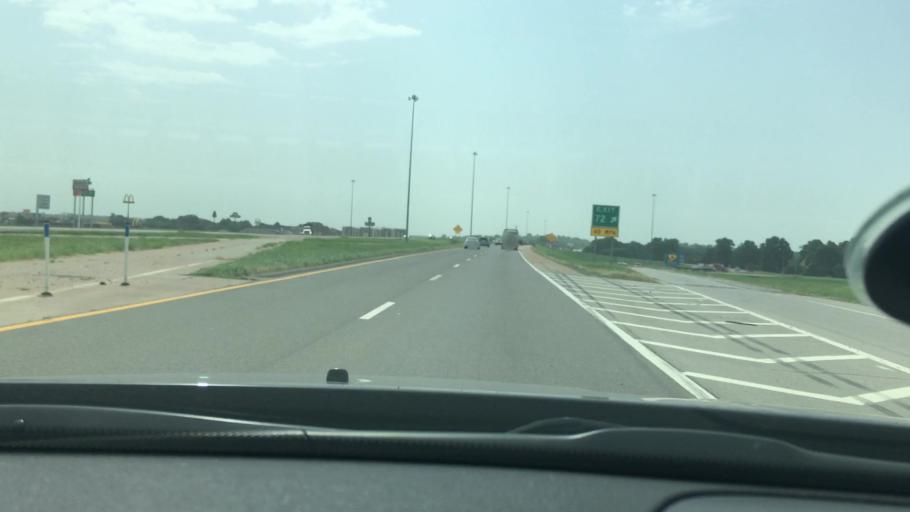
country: US
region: Oklahoma
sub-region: Garvin County
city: Pauls Valley
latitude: 34.7427
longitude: -97.2663
